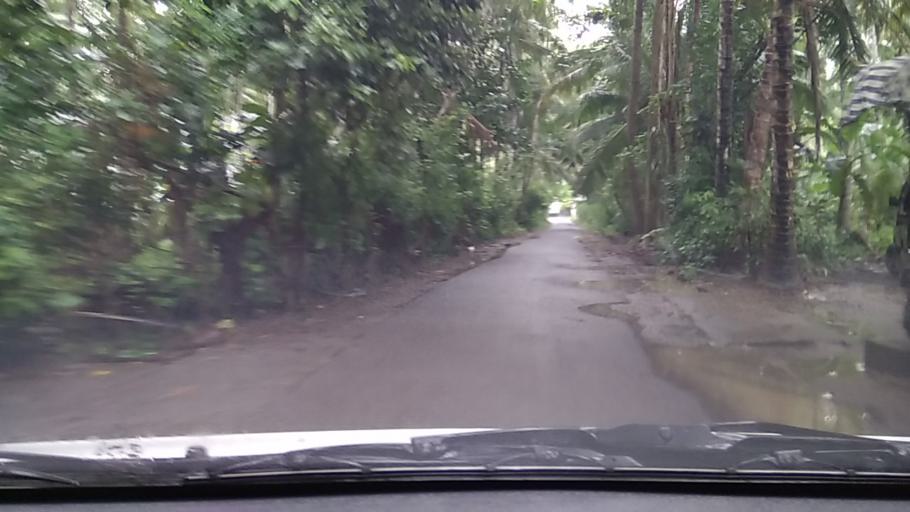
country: ID
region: Bali
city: Banjar Bugbug
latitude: -8.5076
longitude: 115.5781
